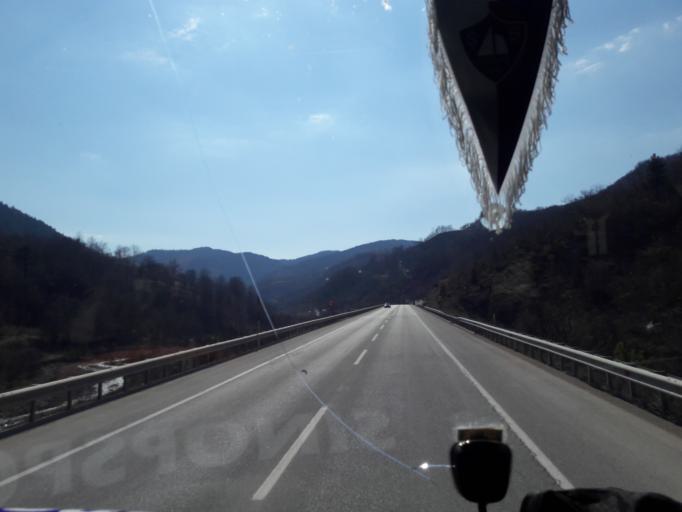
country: TR
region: Sinop
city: Erfelek
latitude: 41.7120
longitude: 34.9291
